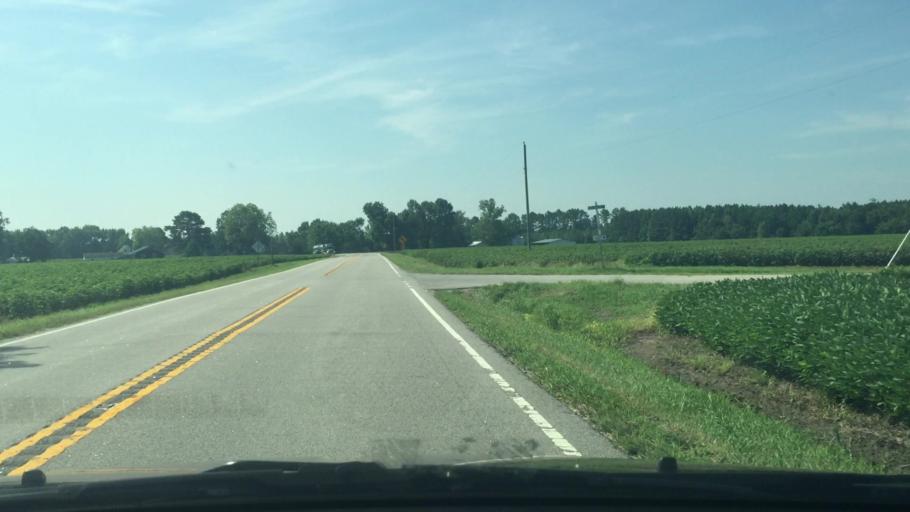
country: US
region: Virginia
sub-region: Southampton County
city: Courtland
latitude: 36.8460
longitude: -77.1326
